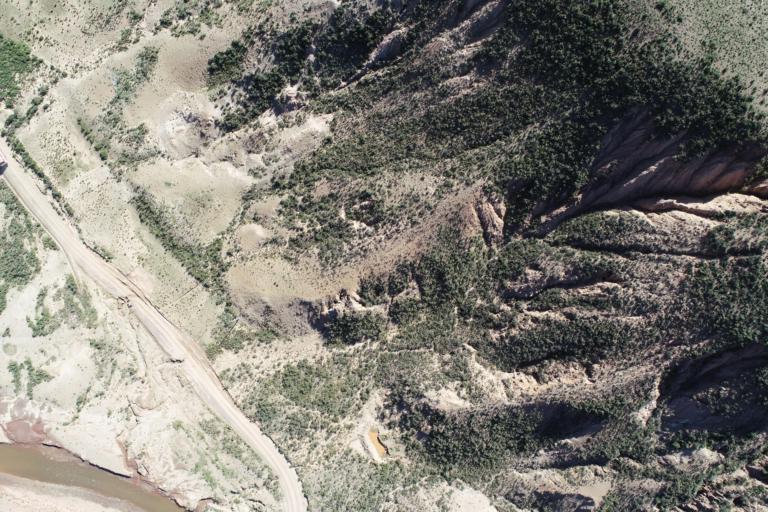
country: BO
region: La Paz
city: Curahuara de Carangas
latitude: -17.3042
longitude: -68.4893
